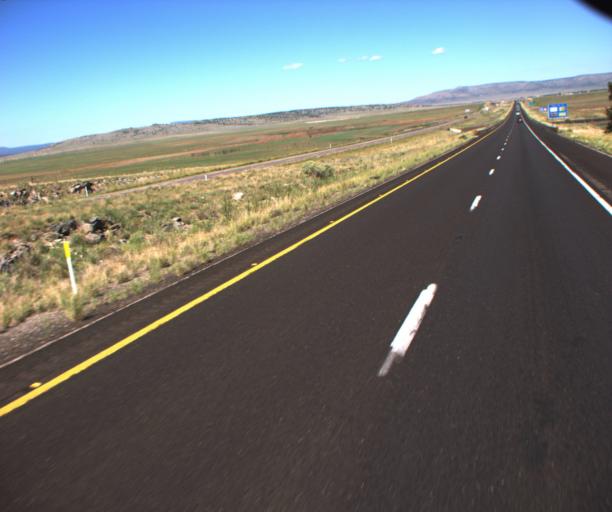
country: US
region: Arizona
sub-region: Yavapai County
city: Paulden
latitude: 35.2962
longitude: -112.8309
